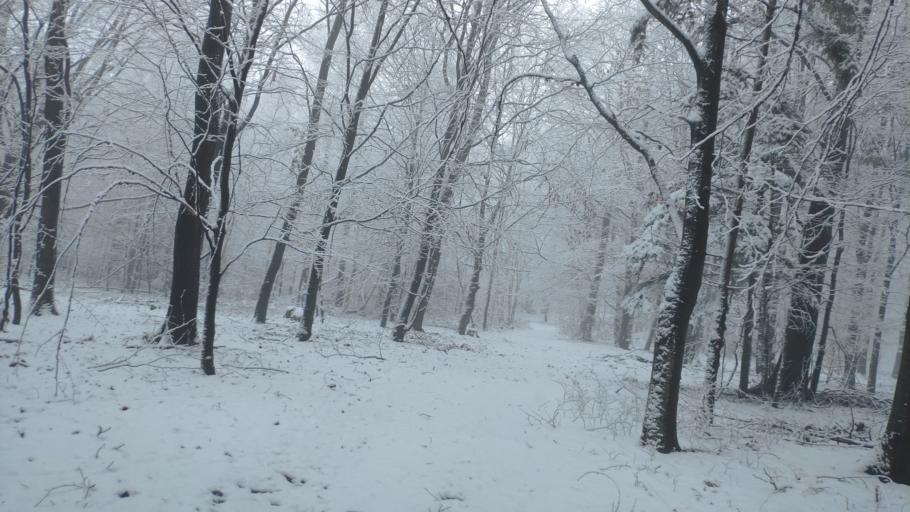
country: SK
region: Kosicky
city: Moldava nad Bodvou
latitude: 48.7395
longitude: 21.0931
